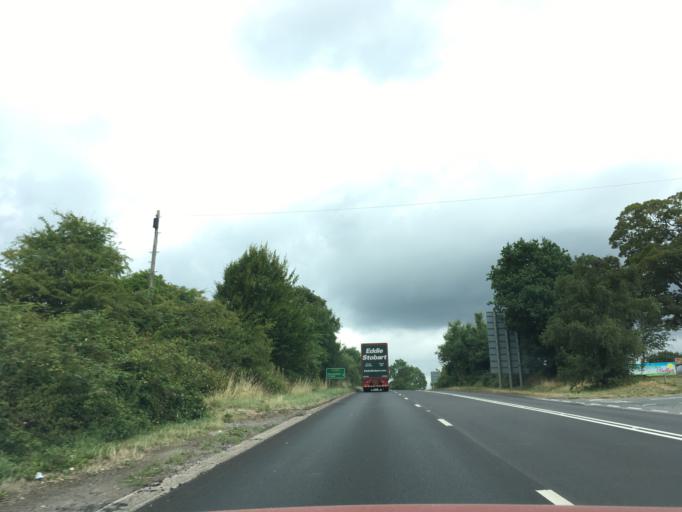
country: GB
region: Wales
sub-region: Torfaen County Borough
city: New Inn
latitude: 51.7230
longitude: -2.9892
